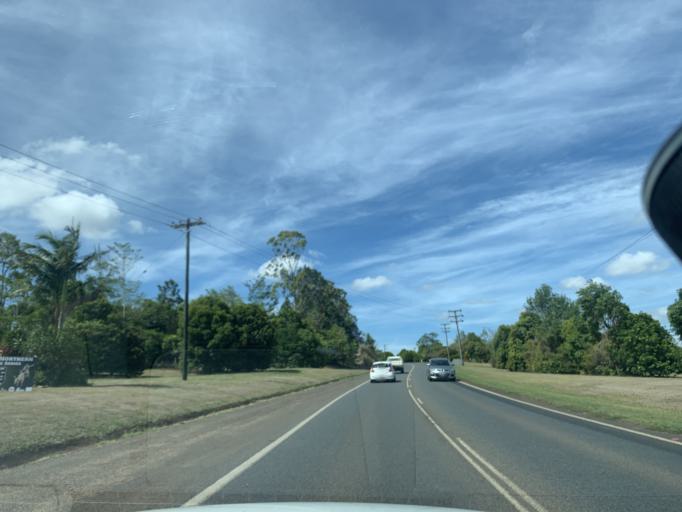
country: AU
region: Queensland
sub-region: Tablelands
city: Atherton
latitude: -17.2521
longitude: 145.4774
